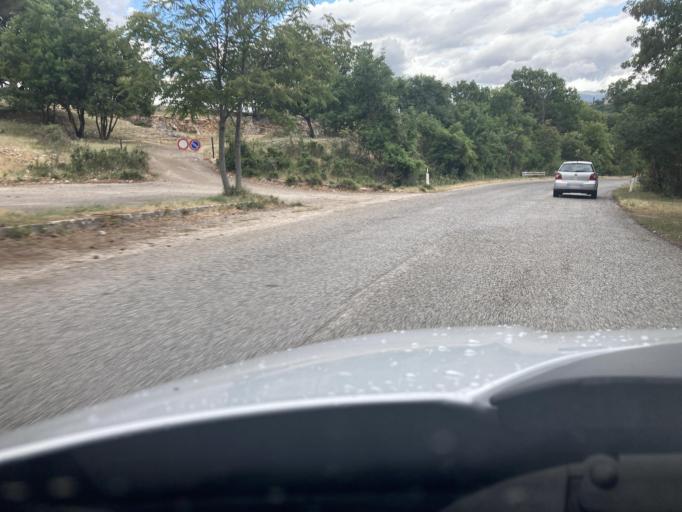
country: IT
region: Abruzzo
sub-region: Provincia dell' Aquila
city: San Panfilo d'Ocre
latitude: 42.2824
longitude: 13.4724
